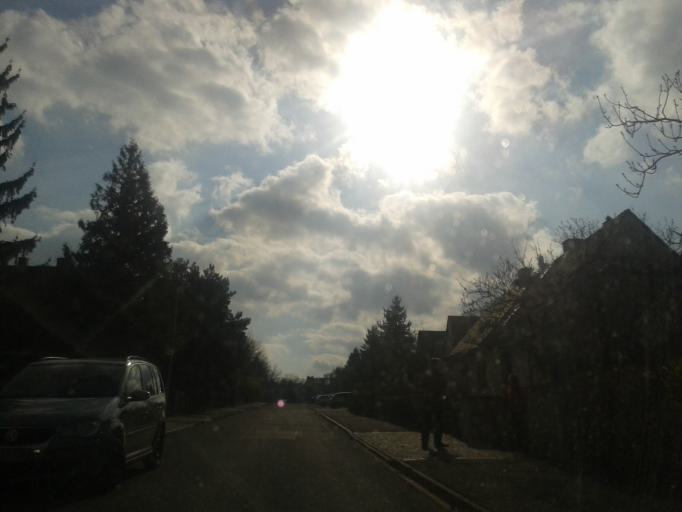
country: DE
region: Saxony
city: Dresden
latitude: 51.0234
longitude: 13.7556
